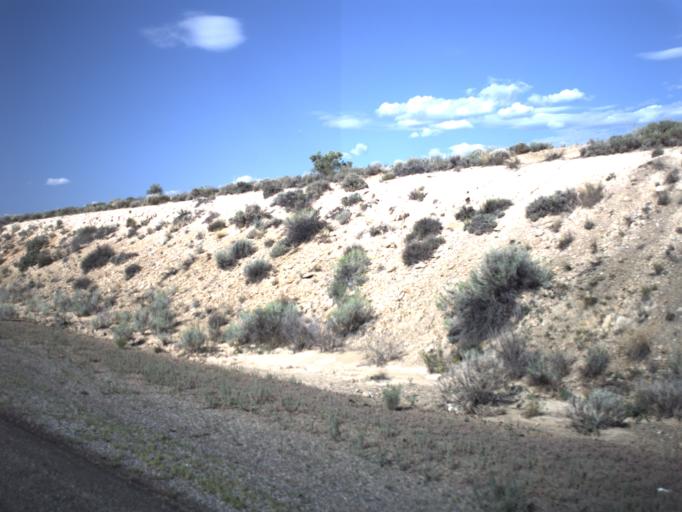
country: US
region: Utah
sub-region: Emery County
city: Huntington
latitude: 39.4049
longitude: -110.8869
